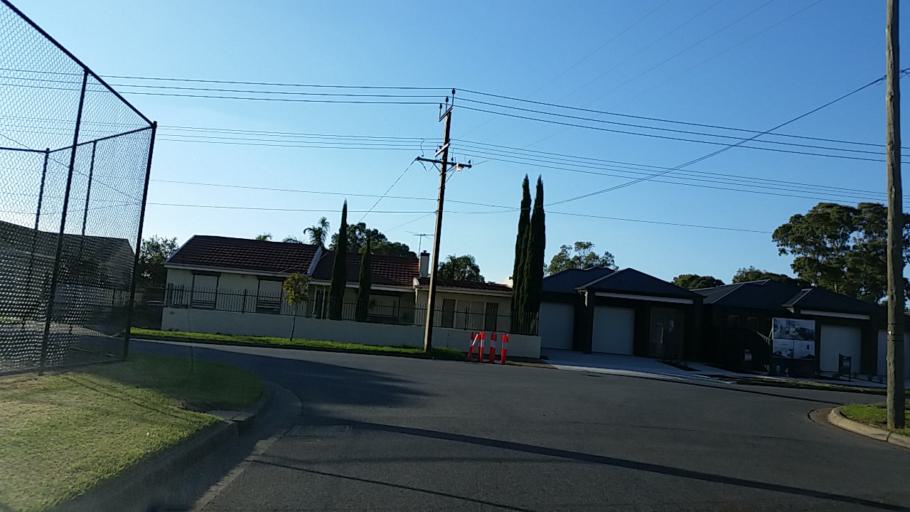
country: AU
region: South Australia
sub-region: Charles Sturt
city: Woodville West
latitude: -34.8900
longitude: 138.5280
